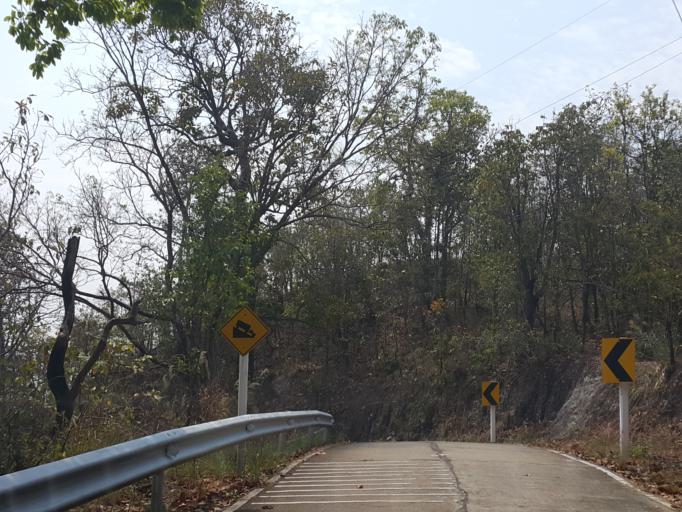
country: TH
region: Lampang
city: Mueang Pan
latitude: 18.8136
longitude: 99.4752
